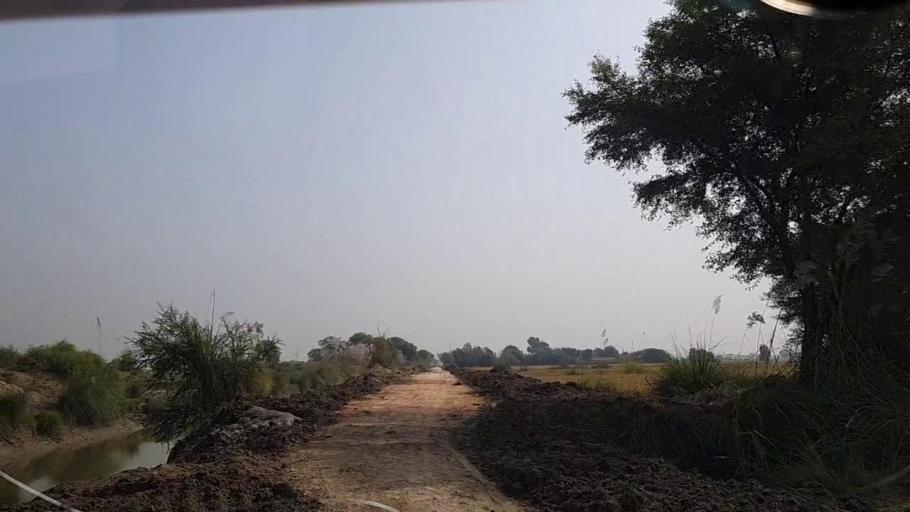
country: PK
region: Sindh
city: Shikarpur
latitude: 27.9203
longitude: 68.5800
